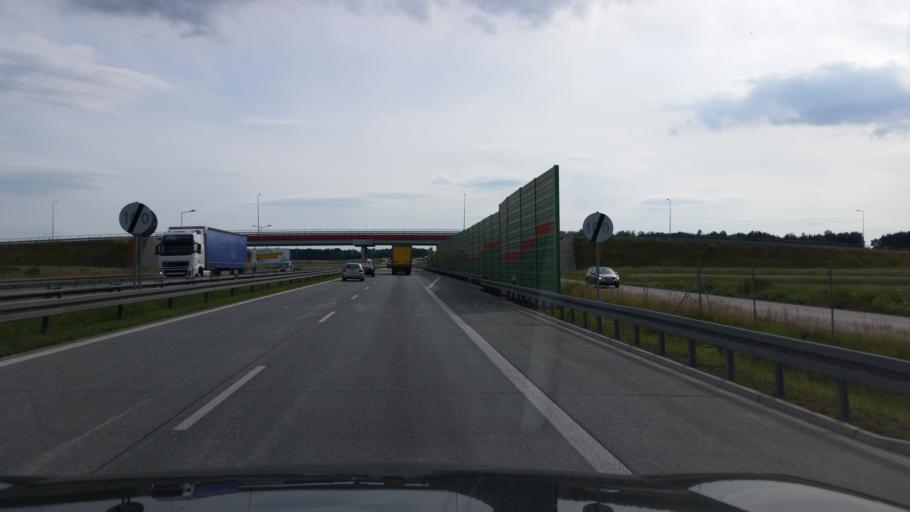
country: PL
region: Lodz Voivodeship
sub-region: Powiat tomaszowski
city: Czerniewice
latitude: 51.6950
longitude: 20.2138
